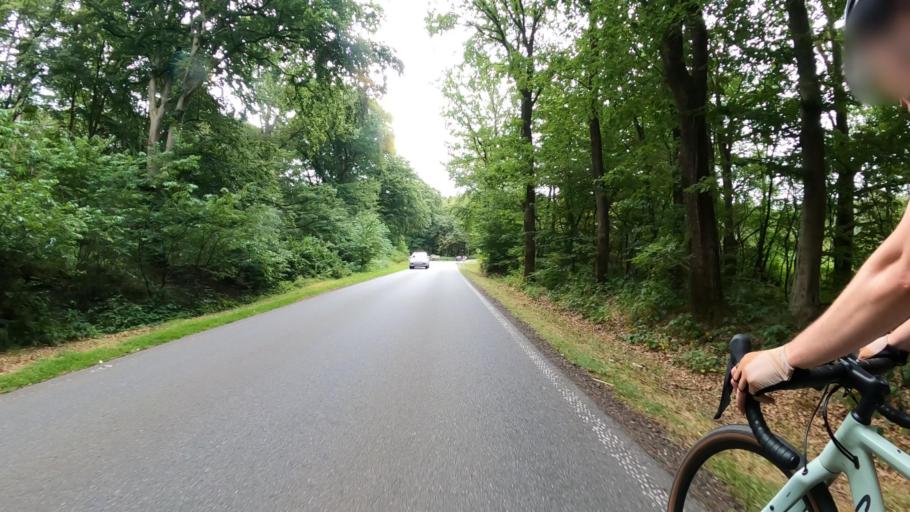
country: DE
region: Schleswig-Holstein
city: Bark
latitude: 53.9500
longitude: 10.1405
